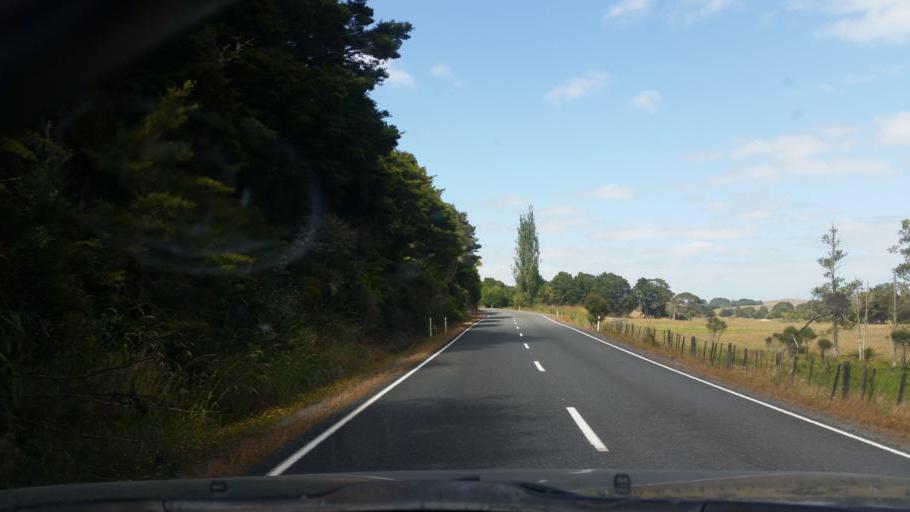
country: NZ
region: Northland
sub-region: Whangarei
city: Ruakaka
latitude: -35.9731
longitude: 174.2884
